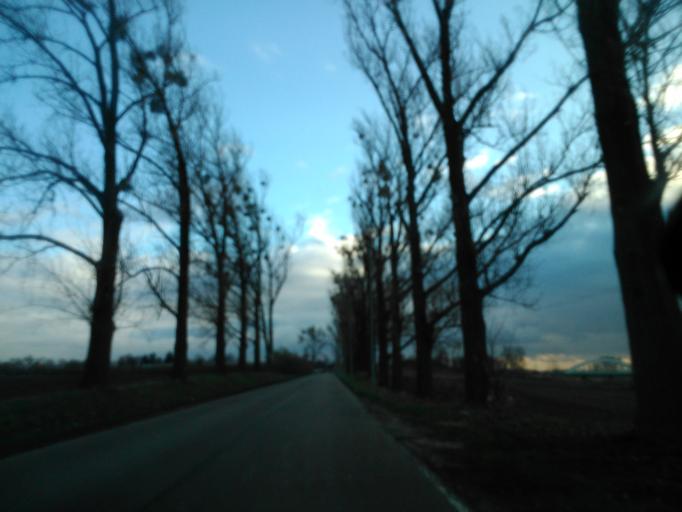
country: PL
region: Masovian Voivodeship
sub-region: Powiat warszawski zachodni
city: Blonie
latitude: 52.2105
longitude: 20.6557
